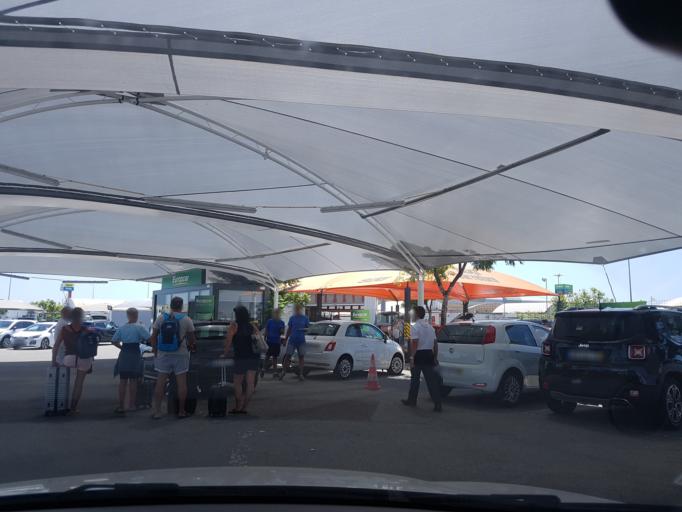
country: PT
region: Faro
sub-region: Faro
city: Faro
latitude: 37.0215
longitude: -7.9645
